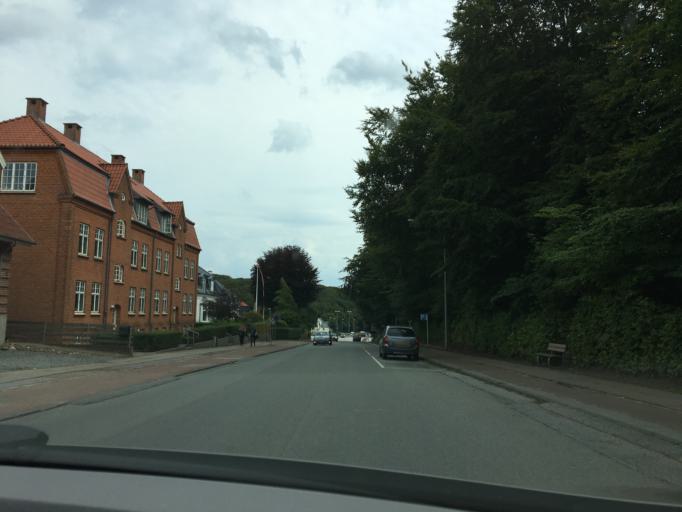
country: DK
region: Central Jutland
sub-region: Skive Kommune
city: Skive
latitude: 56.5698
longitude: 9.0327
